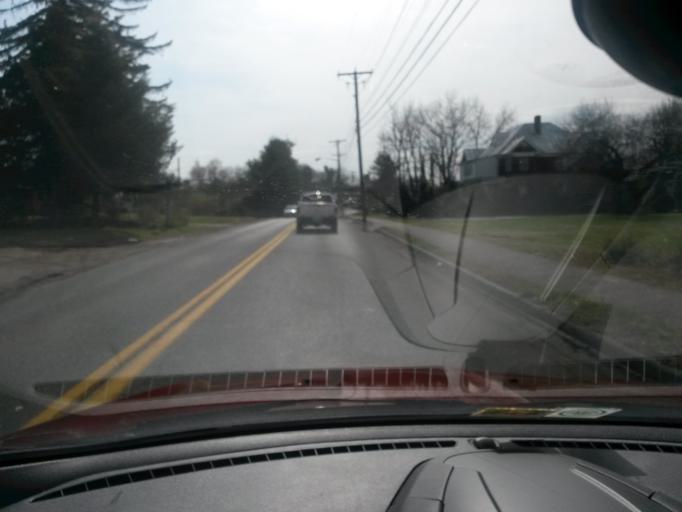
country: US
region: Virginia
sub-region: City of Roanoke
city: Roanoke
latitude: 37.2991
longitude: -79.9741
